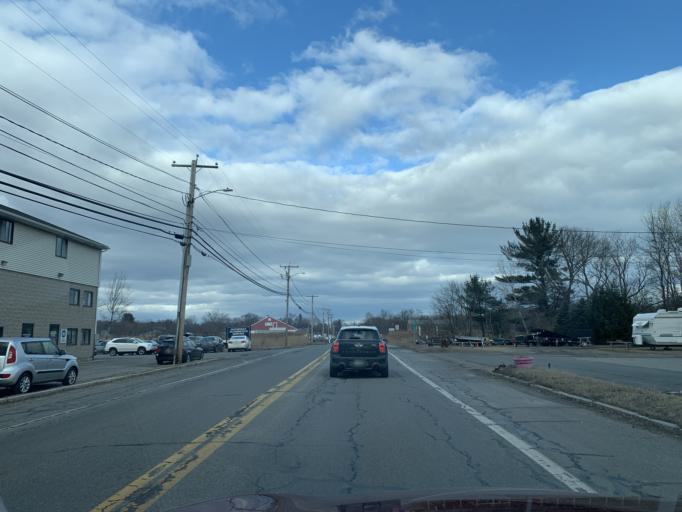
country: US
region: Massachusetts
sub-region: Essex County
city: Salisbury
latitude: 42.8326
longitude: -70.8625
